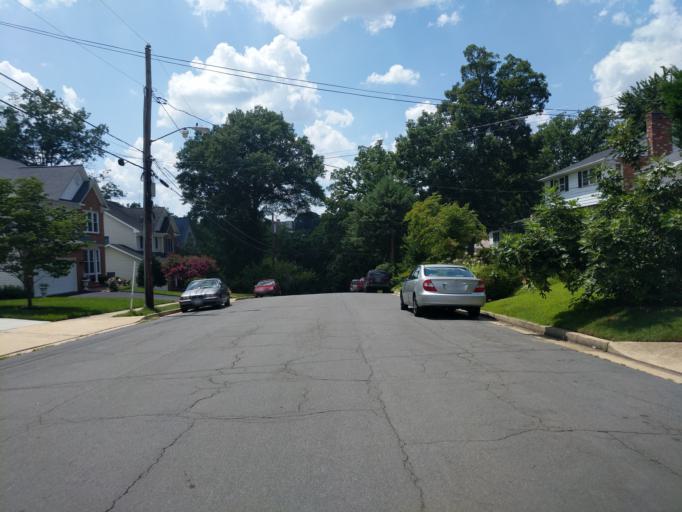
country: US
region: Virginia
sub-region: Fairfax County
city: Baileys Crossroads
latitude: 38.8587
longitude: -77.1099
